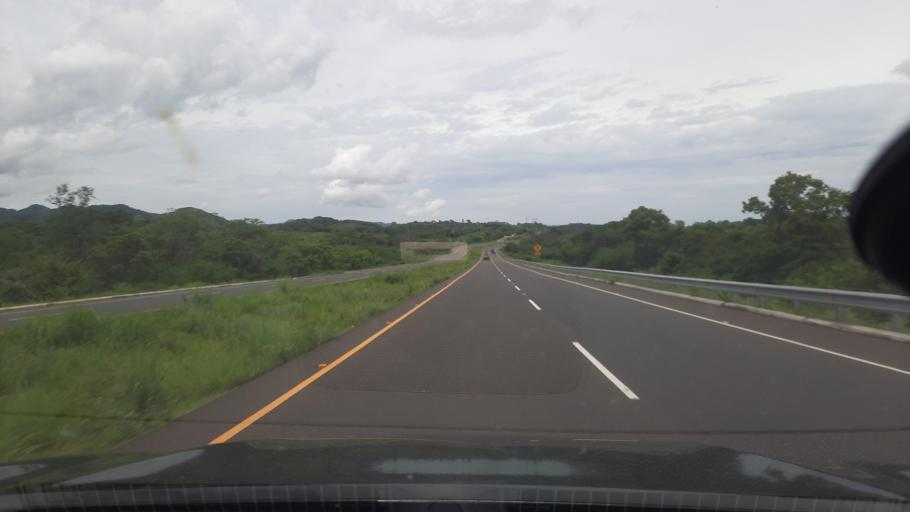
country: HN
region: Valle
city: Aramecina
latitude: 13.7807
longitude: -87.6994
